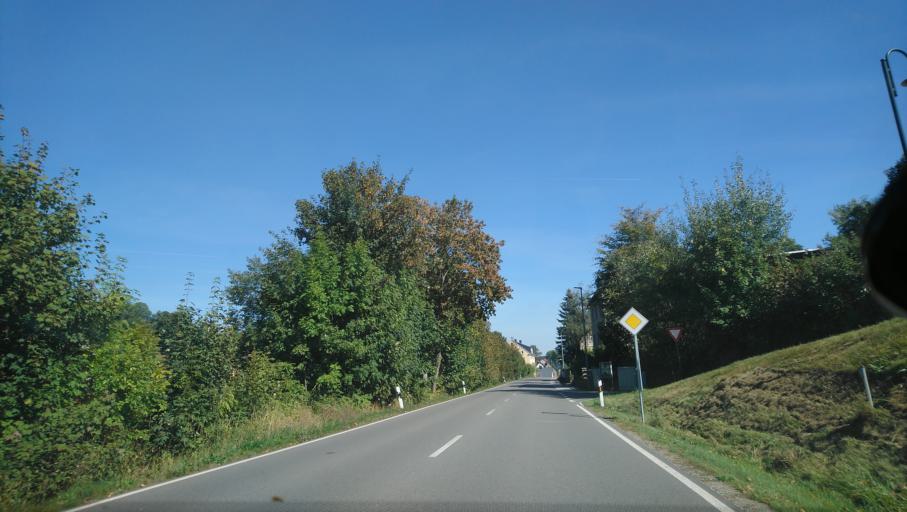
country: DE
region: Saxony
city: Crottendorf
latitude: 50.5073
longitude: 12.9805
